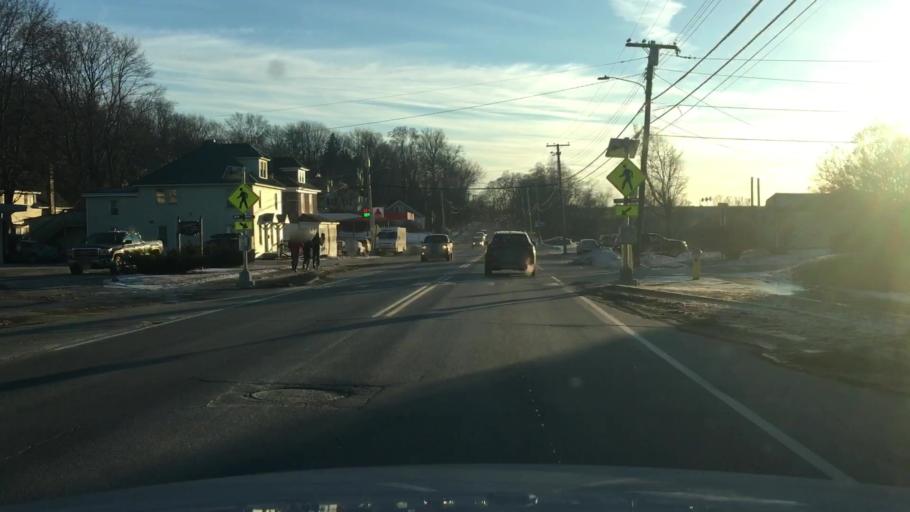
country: US
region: Maine
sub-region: Penobscot County
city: Brewer
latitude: 44.7913
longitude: -68.7686
